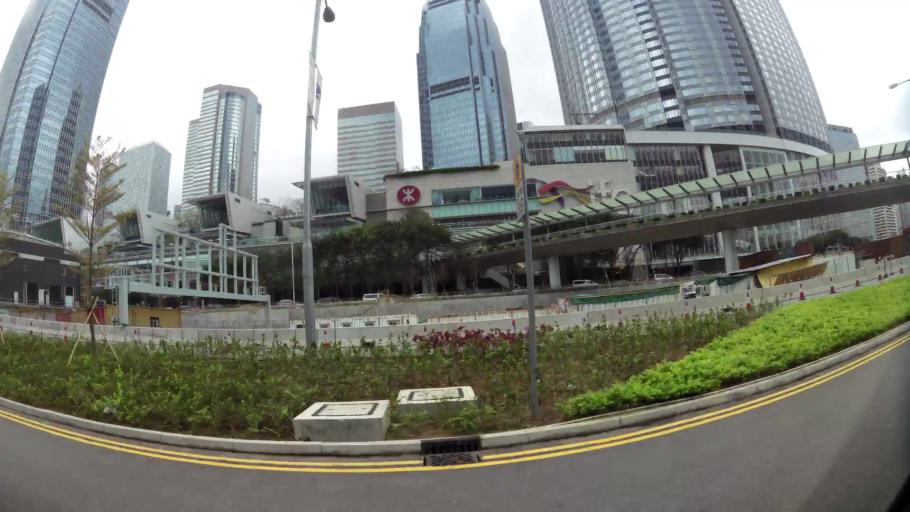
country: HK
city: Hong Kong
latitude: 22.2870
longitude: 114.1583
